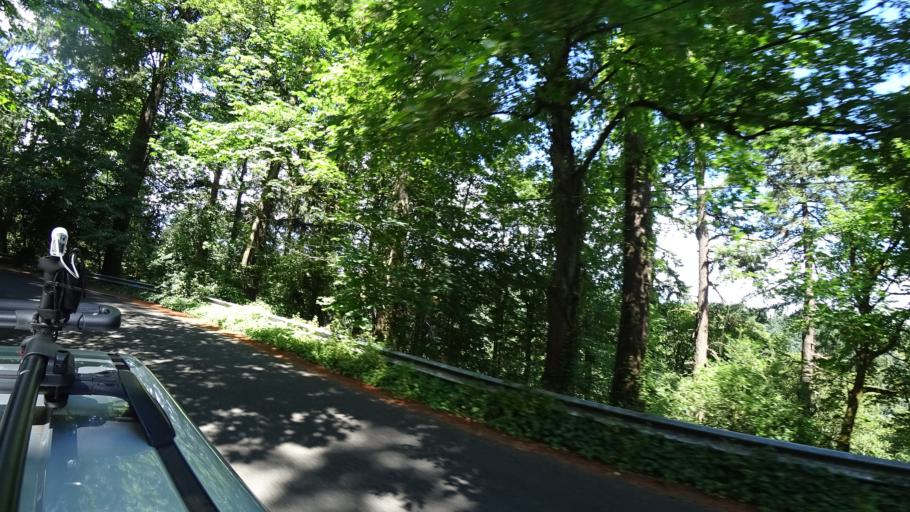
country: US
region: Oregon
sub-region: Multnomah County
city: Portland
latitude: 45.5099
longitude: -122.7053
